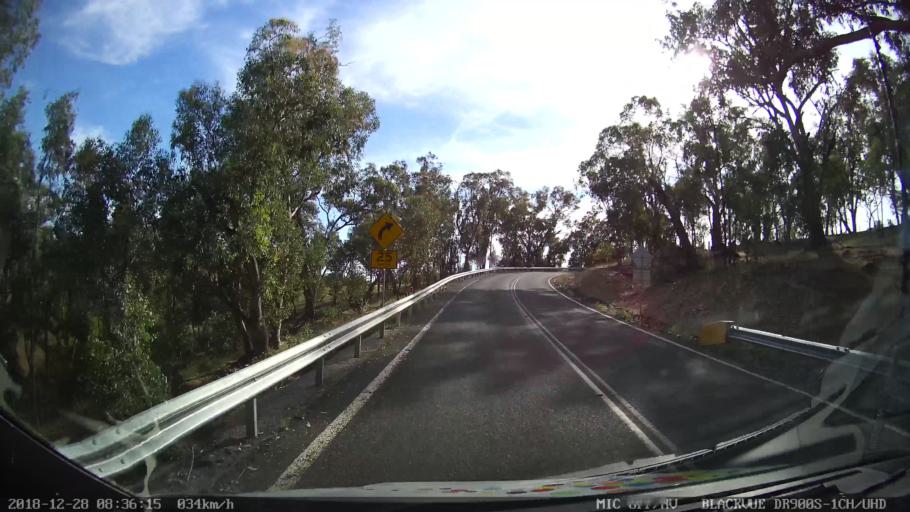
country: AU
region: New South Wales
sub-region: Blayney
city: Blayney
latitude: -33.9877
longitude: 149.3107
